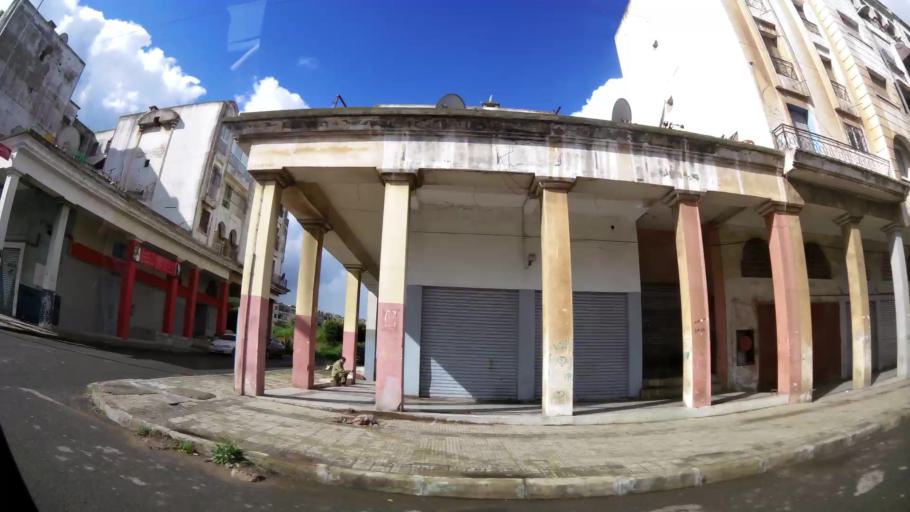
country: MA
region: Grand Casablanca
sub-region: Mediouna
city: Tit Mellil
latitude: 33.5749
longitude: -7.5293
